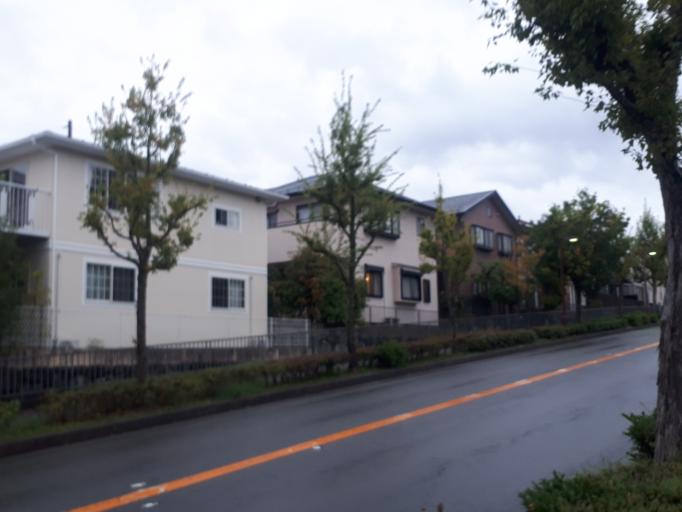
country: JP
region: Kyoto
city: Muko
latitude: 34.9830
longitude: 135.6762
